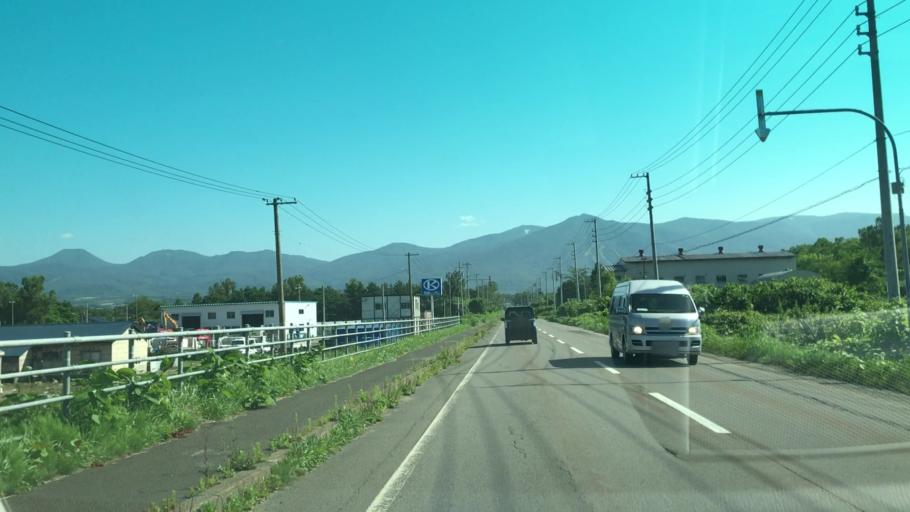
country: JP
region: Hokkaido
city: Iwanai
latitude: 43.0128
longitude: 140.5439
